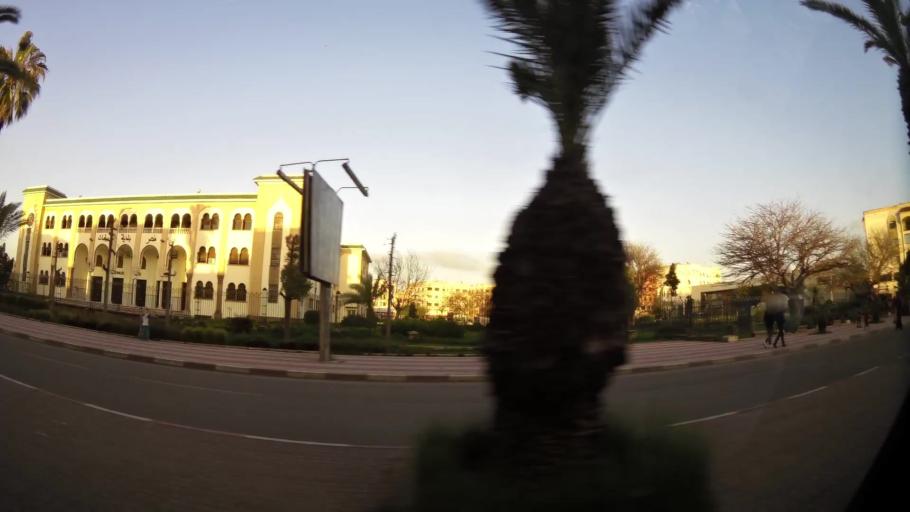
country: MA
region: Chaouia-Ouardigha
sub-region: Settat Province
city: Settat
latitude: 32.9998
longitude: -7.6201
